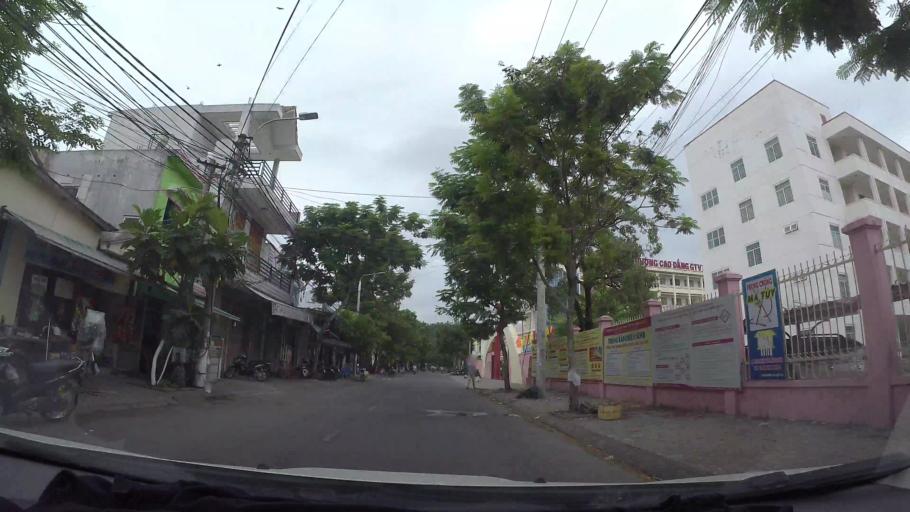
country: VN
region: Da Nang
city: Lien Chieu
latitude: 16.1220
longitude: 108.1180
